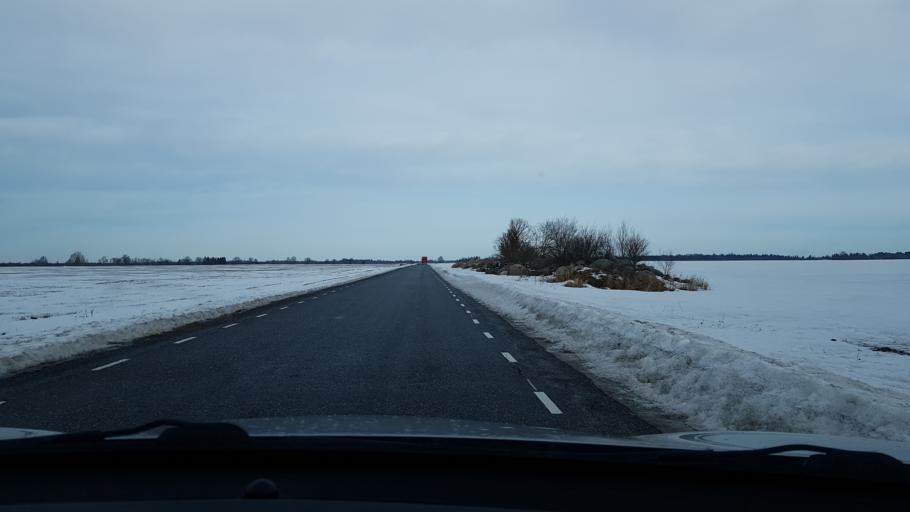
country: EE
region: Jaervamaa
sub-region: Paide linn
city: Paide
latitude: 58.8704
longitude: 25.6691
